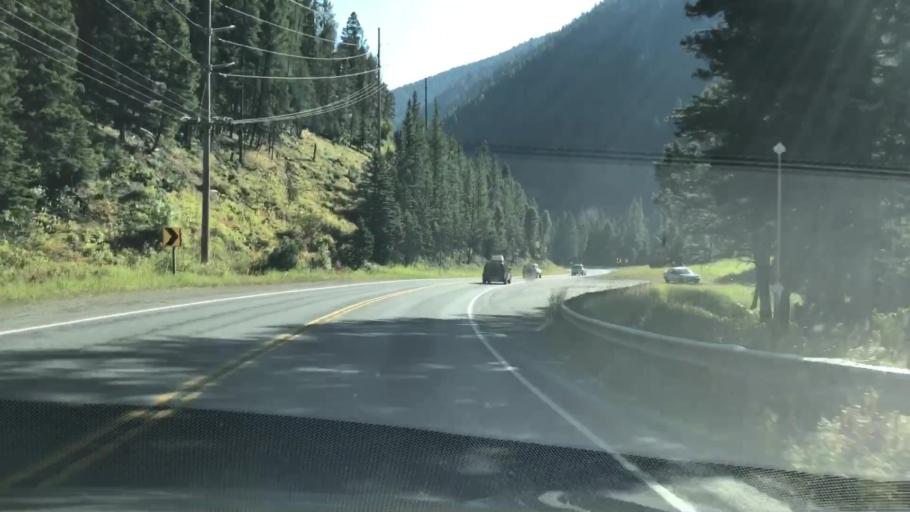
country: US
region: Montana
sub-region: Gallatin County
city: Big Sky
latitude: 45.3770
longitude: -111.1739
